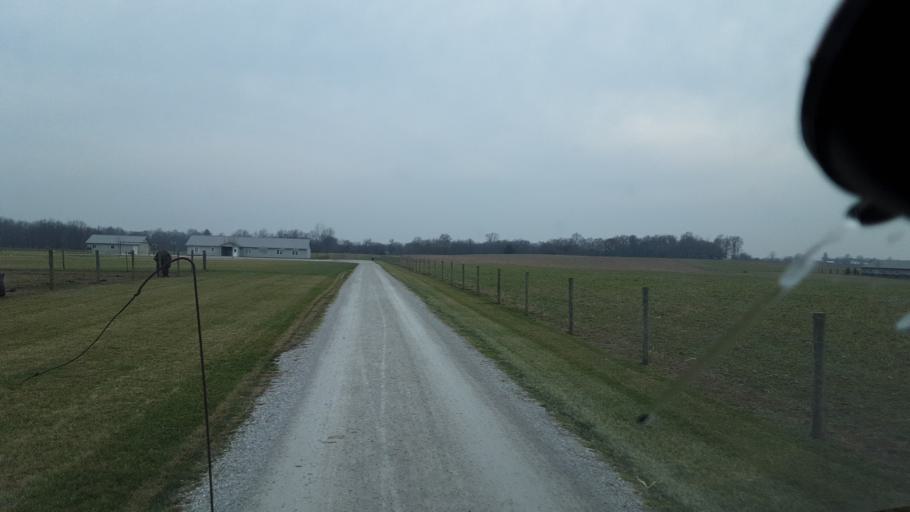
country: US
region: Indiana
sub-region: Elkhart County
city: Middlebury
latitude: 41.6977
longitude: -85.6206
